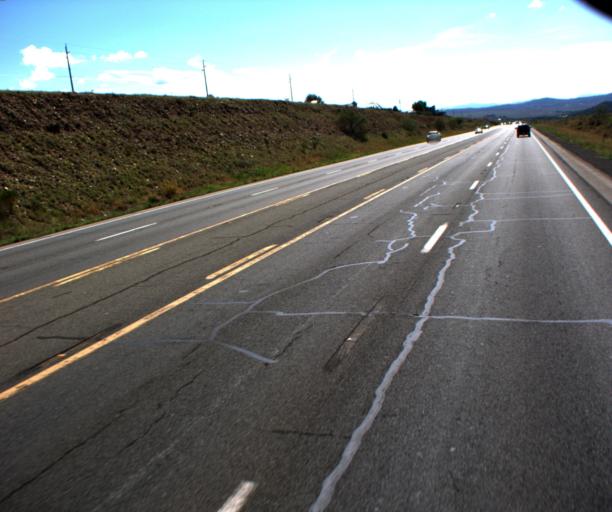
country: US
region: Arizona
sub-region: Yavapai County
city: Prescott Valley
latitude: 34.5821
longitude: -112.3059
